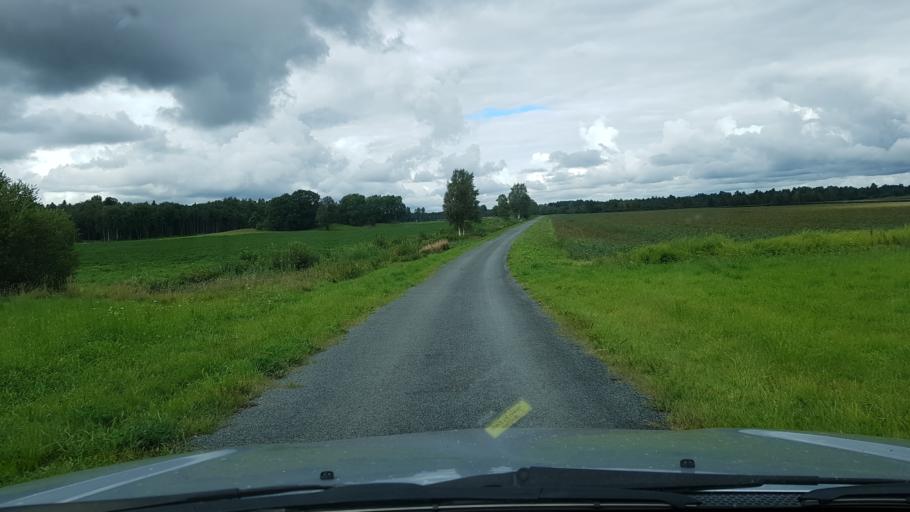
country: EE
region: Harju
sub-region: Raasiku vald
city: Arukula
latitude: 59.2772
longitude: 25.0810
